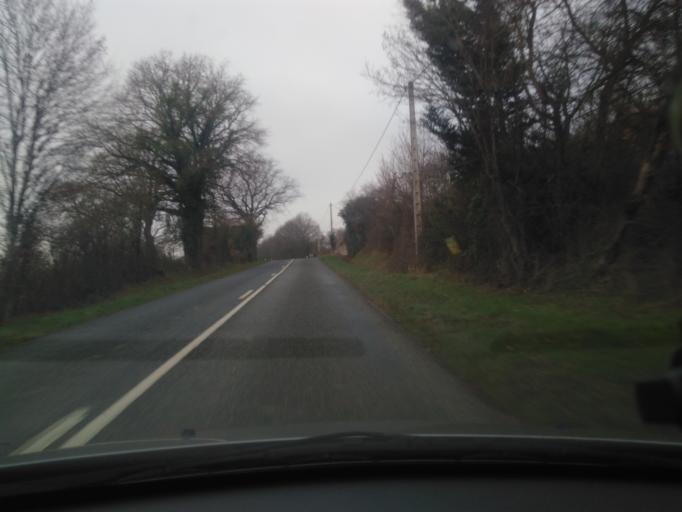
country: FR
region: Centre
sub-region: Departement du Cher
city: Chateaumeillant
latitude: 46.6338
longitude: 2.1688
